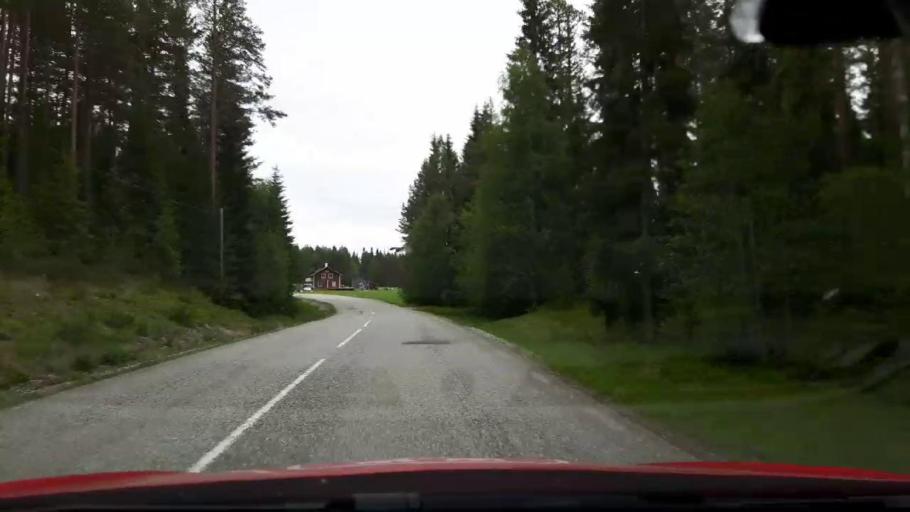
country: SE
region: Jaemtland
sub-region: Ragunda Kommun
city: Hammarstrand
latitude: 63.2450
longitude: 15.9110
